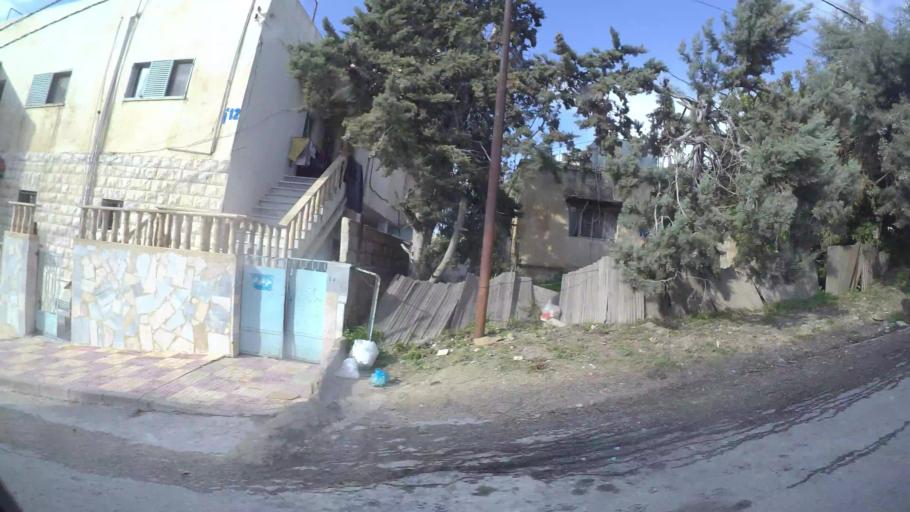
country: JO
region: Amman
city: Al Jubayhah
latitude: 32.0192
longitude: 35.8470
